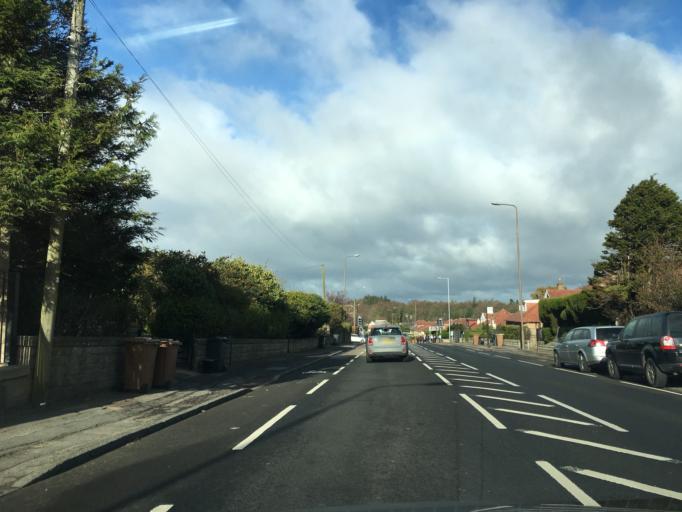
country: GB
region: Scotland
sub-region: Edinburgh
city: Colinton
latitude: 55.9021
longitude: -3.2152
